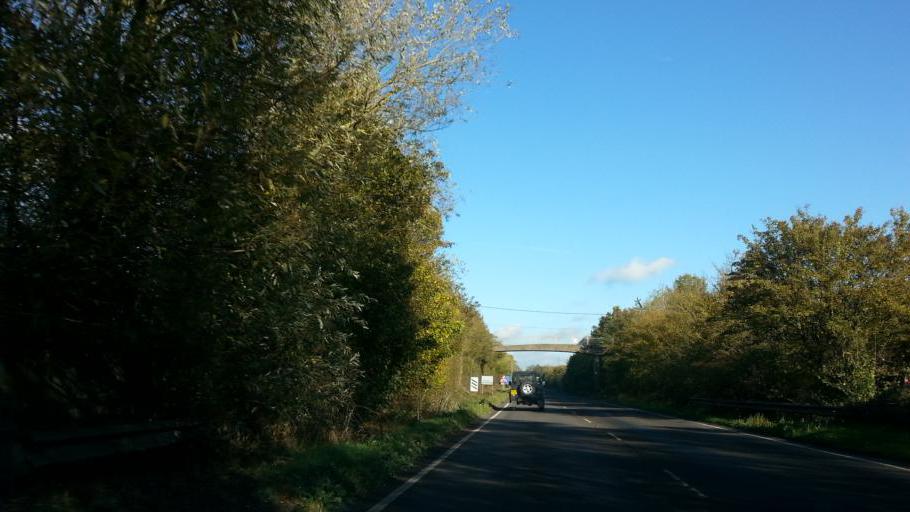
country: GB
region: England
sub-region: Suffolk
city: Bungay
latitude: 52.4574
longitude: 1.4283
